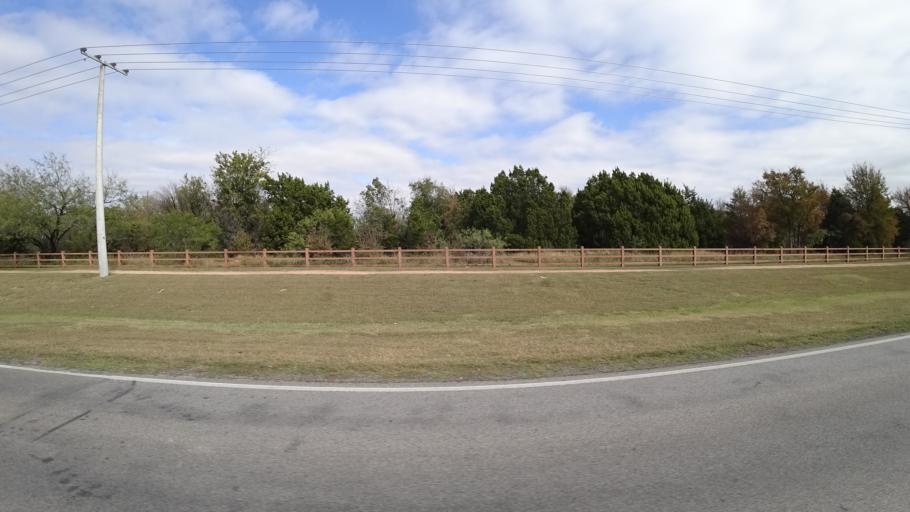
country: US
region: Texas
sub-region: Williamson County
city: Brushy Creek
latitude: 30.5306
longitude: -97.7216
